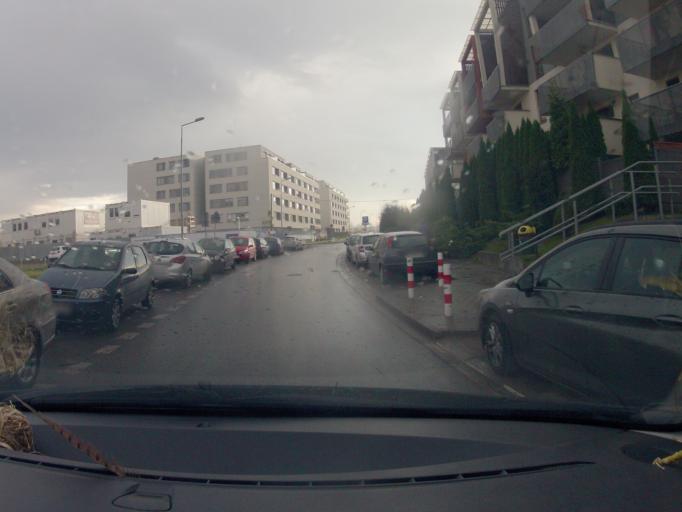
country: PL
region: Lesser Poland Voivodeship
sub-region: Krakow
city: Sidzina
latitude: 50.0126
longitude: 19.8901
